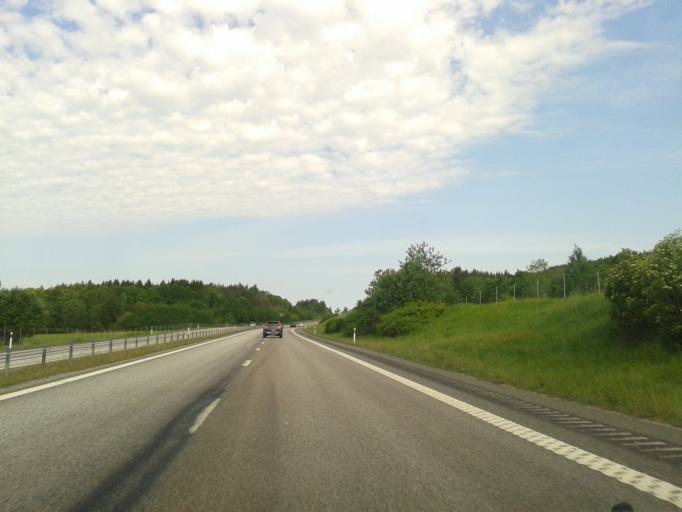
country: SE
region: Vaestra Goetaland
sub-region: Munkedals Kommun
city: Munkedal
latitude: 58.5429
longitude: 11.5217
